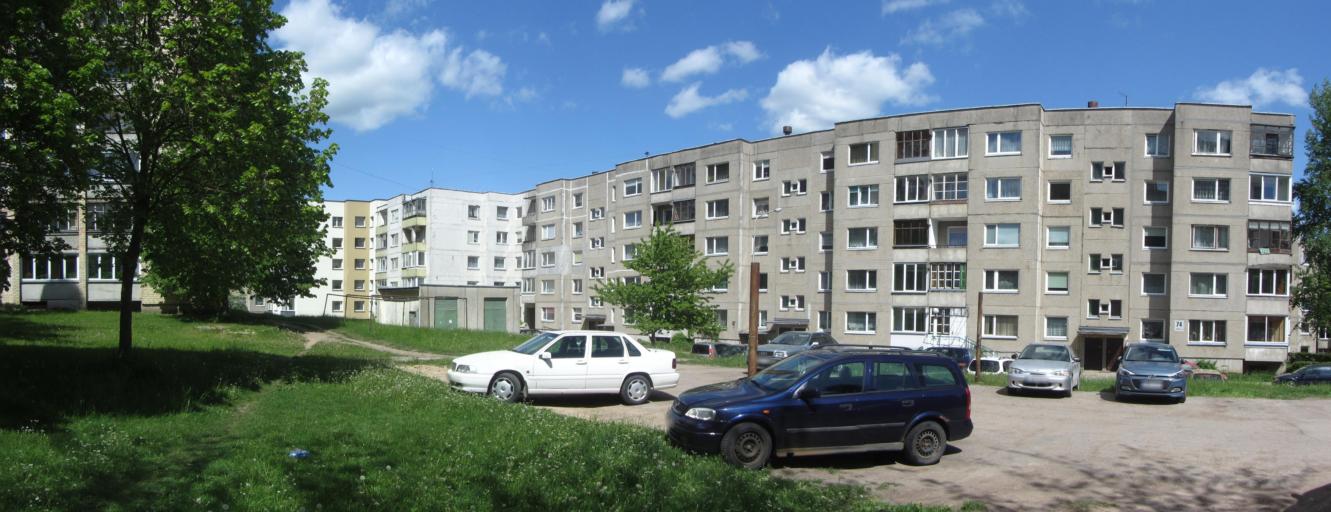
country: LT
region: Utenos apskritis
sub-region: Utena
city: Utena
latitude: 55.5049
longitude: 25.5851
